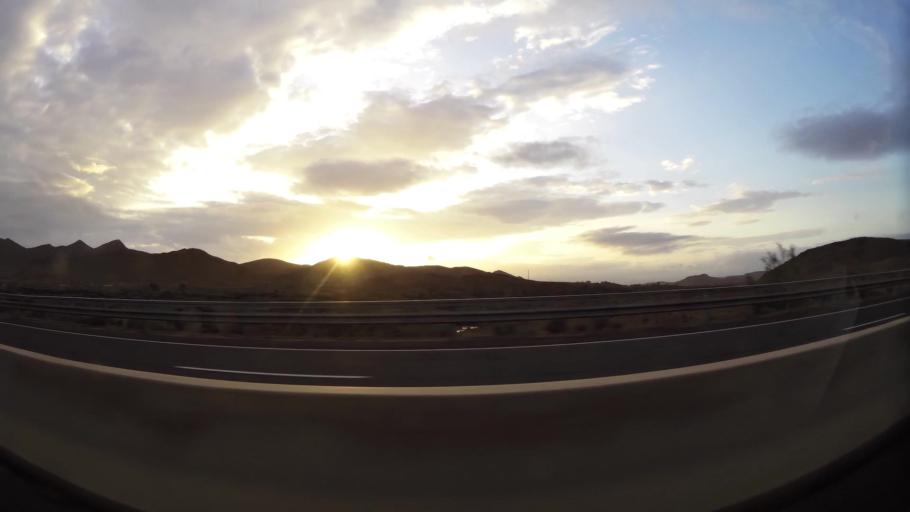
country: MA
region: Oriental
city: Taourirt
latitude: 34.4839
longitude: -2.9839
